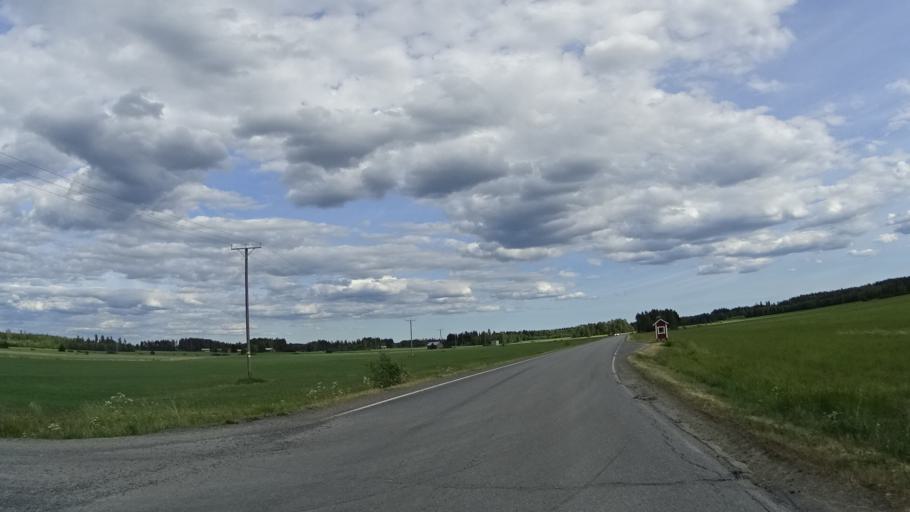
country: FI
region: Haeme
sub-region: Forssa
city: Forssa
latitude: 60.9344
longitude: 23.5743
